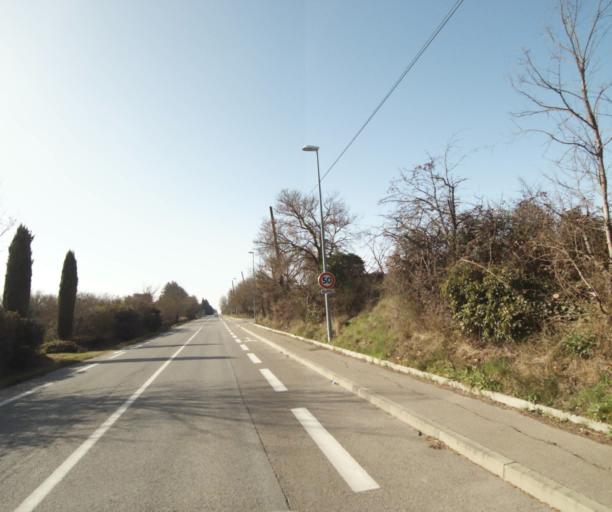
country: FR
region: Provence-Alpes-Cote d'Azur
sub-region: Departement des Bouches-du-Rhone
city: Aix-en-Provence
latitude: 43.5531
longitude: 5.4581
